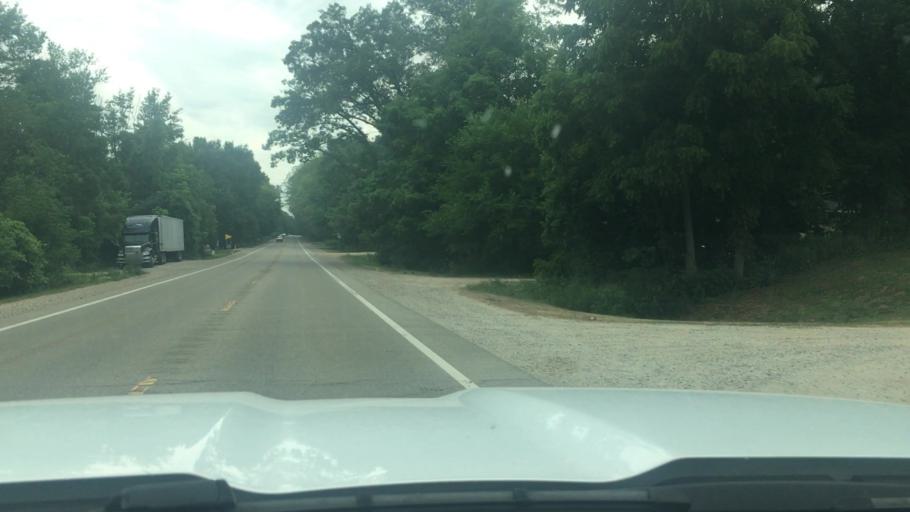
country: US
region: Michigan
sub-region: Ionia County
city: Saranac
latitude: 42.9359
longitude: -85.2245
